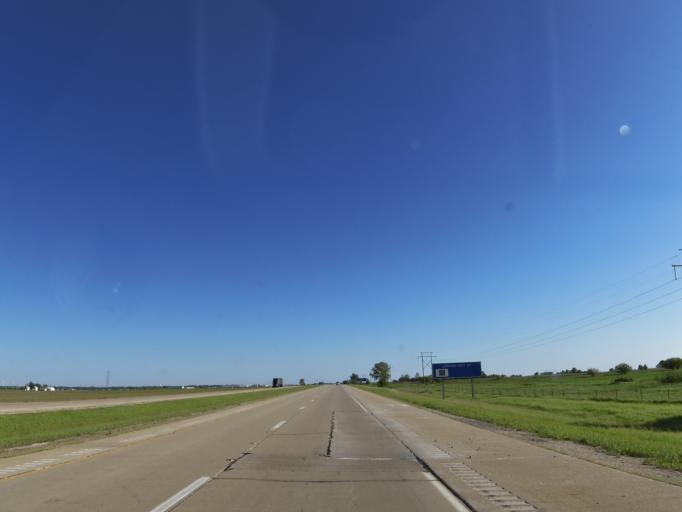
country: US
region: Illinois
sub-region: Woodford County
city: Minonk
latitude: 40.9375
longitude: -89.0568
